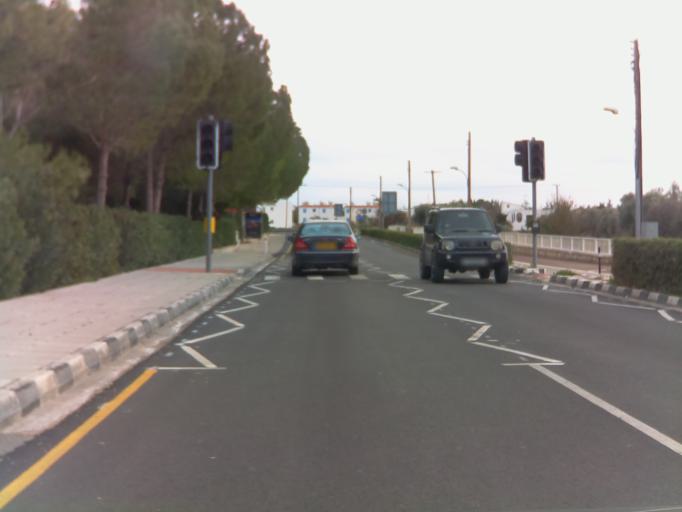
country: CY
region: Pafos
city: Polis
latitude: 35.0356
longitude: 32.4097
